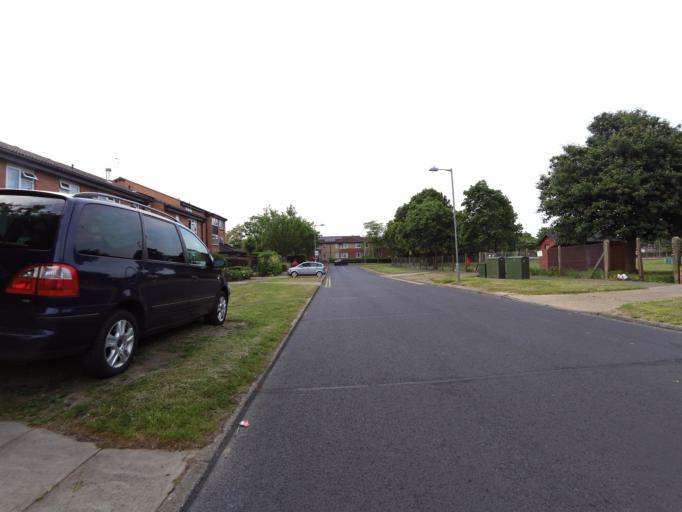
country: GB
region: England
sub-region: Suffolk
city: Ipswich
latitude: 52.0798
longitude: 1.1391
